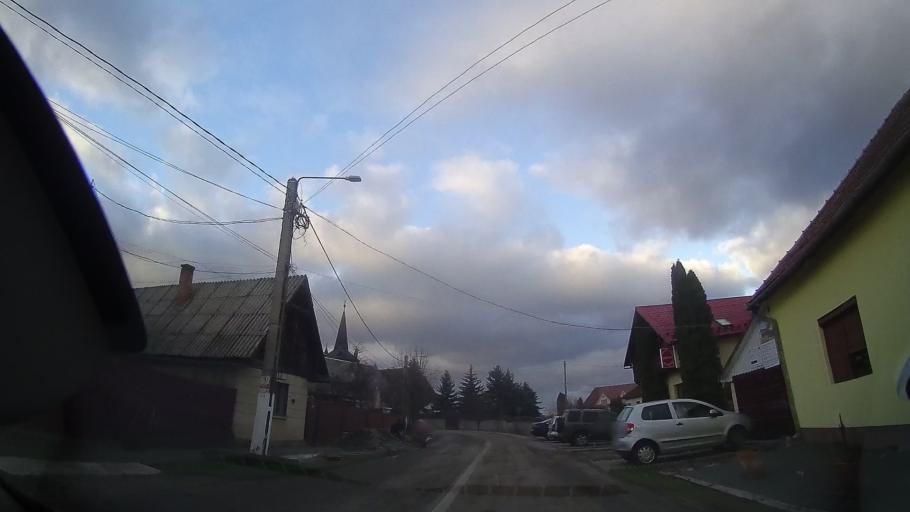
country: RO
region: Cluj
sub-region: Comuna Sancraiu
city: Sancraiu
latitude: 46.8279
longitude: 22.9885
